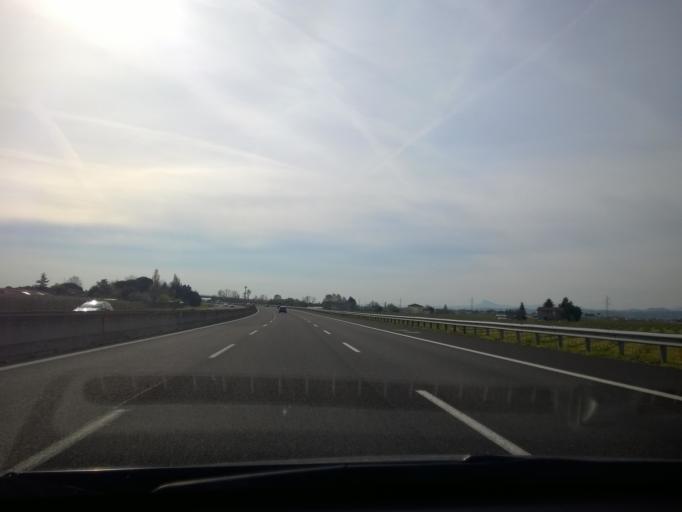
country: IT
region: Emilia-Romagna
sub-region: Forli-Cesena
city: Bagnarola
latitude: 44.1491
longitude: 12.3226
